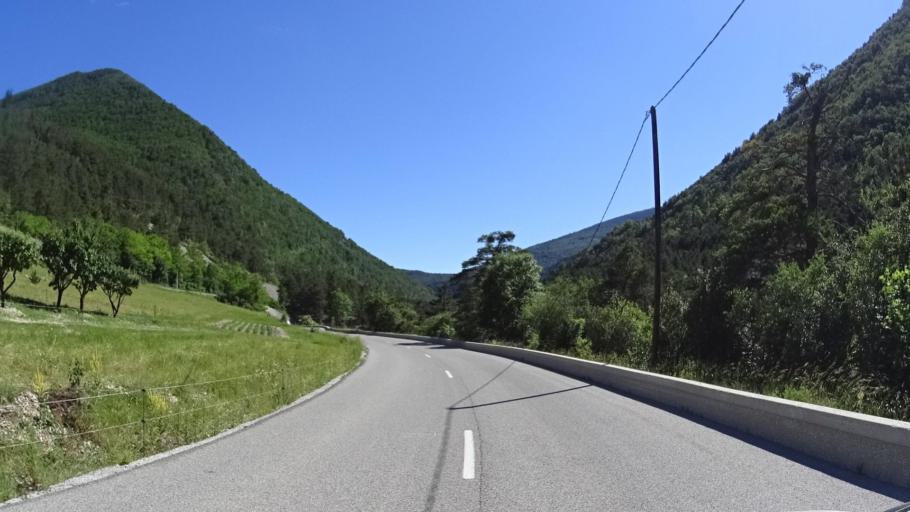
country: FR
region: Provence-Alpes-Cote d'Azur
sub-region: Departement des Alpes-de-Haute-Provence
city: Annot
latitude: 44.0393
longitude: 6.5639
